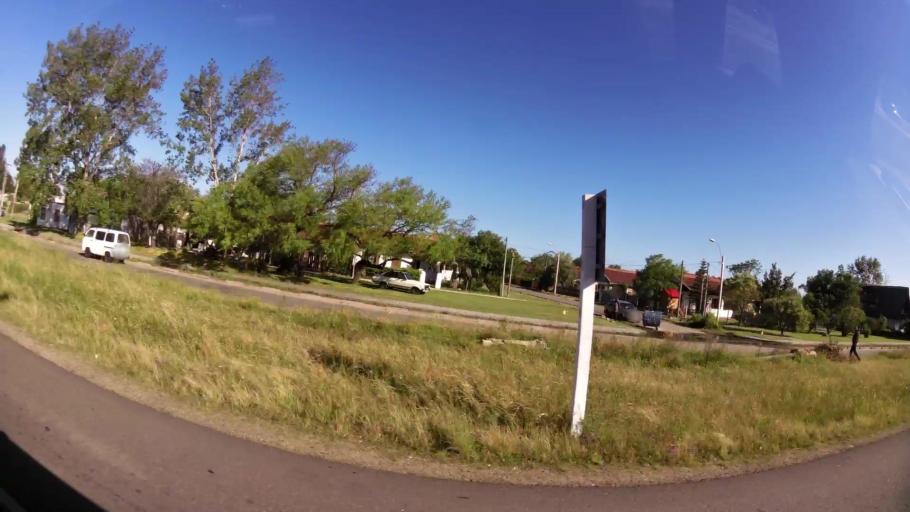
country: UY
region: Canelones
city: Barra de Carrasco
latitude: -34.8695
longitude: -56.0260
